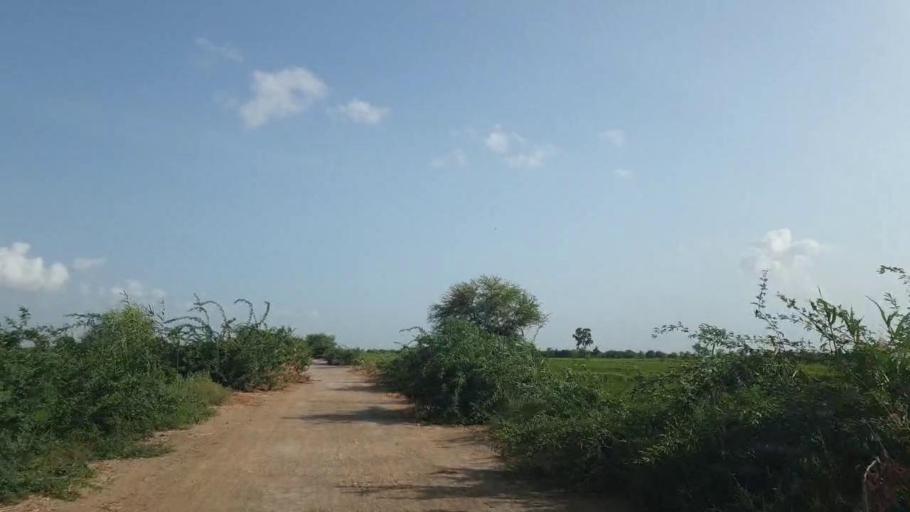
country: PK
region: Sindh
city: Kadhan
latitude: 24.6198
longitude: 69.0958
